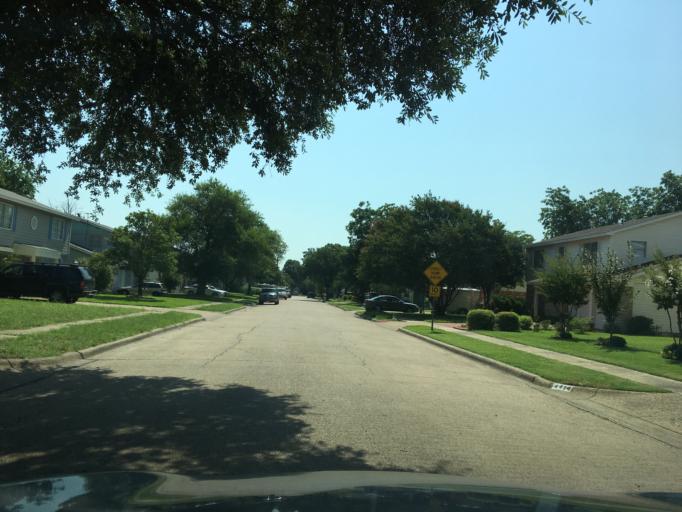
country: US
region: Texas
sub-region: Dallas County
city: Richardson
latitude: 32.9227
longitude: -96.6993
